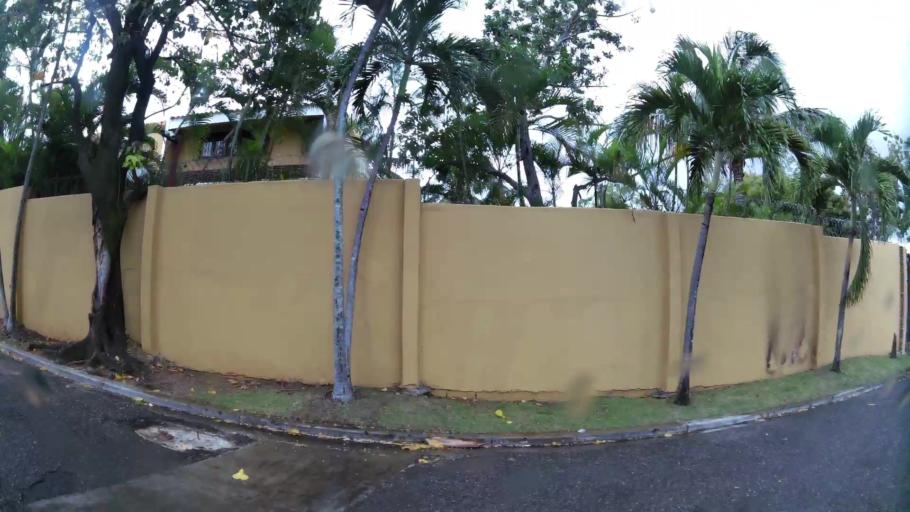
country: DO
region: Nacional
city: La Agustina
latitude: 18.5001
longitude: -69.9376
